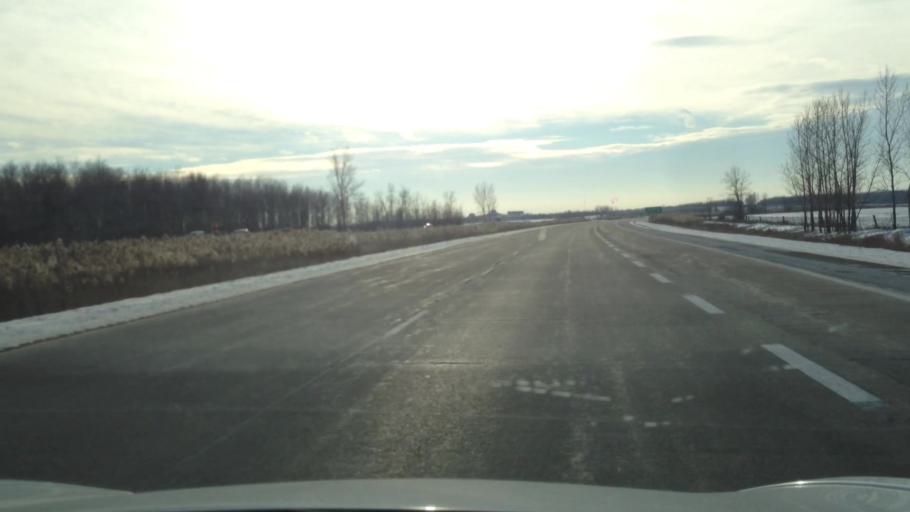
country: CA
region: Ontario
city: Hawkesbury
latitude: 45.4729
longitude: -74.6695
